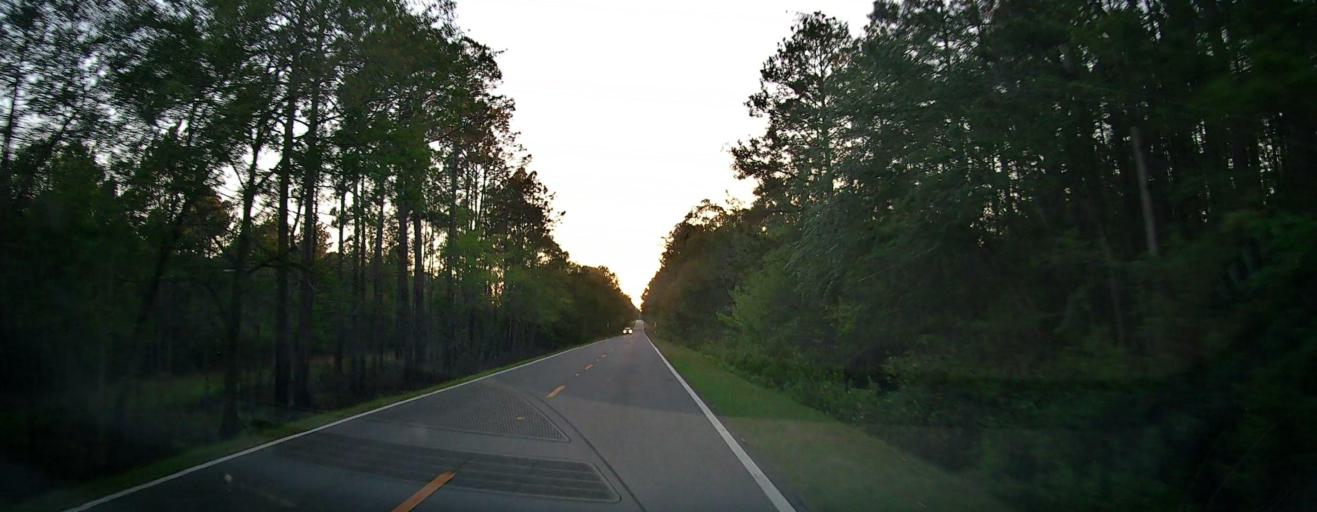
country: US
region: Georgia
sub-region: Wilcox County
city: Rochelle
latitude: 31.7831
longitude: -83.4212
